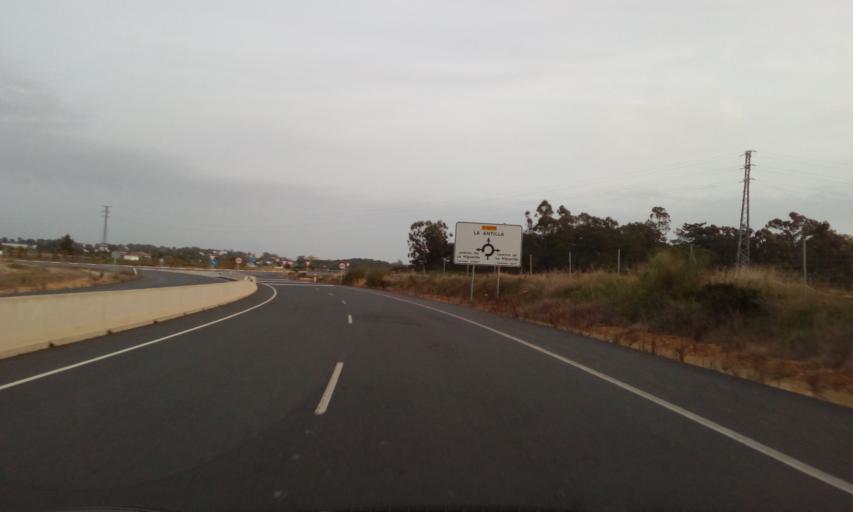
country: ES
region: Andalusia
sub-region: Provincia de Huelva
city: Lepe
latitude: 37.2313
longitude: -7.2308
